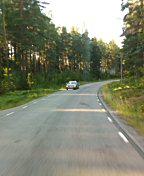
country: SE
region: Uppsala
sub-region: Habo Kommun
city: Balsta
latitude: 59.7008
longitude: 17.5368
